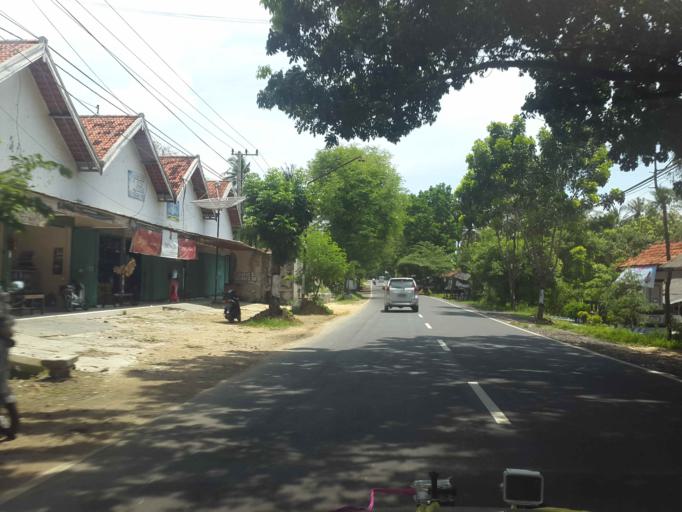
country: ID
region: East Java
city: Ketapang Daja
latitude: -7.1120
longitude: 113.6507
